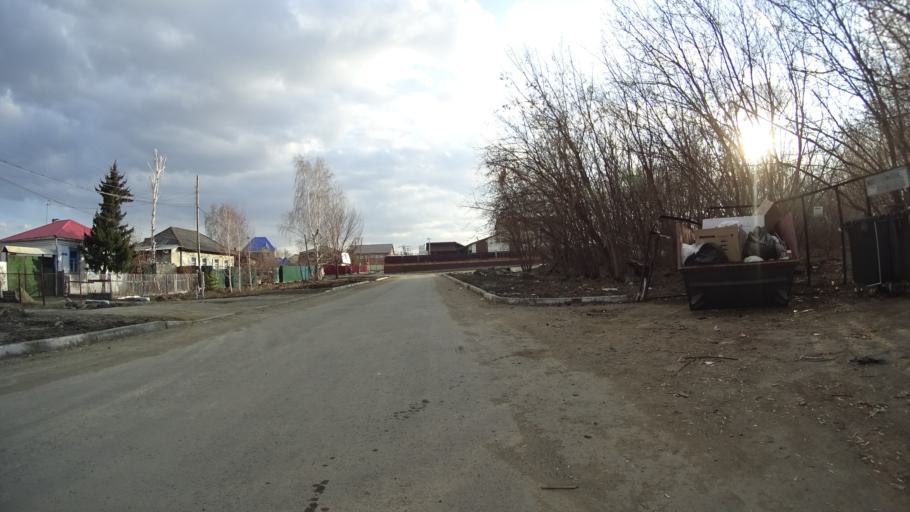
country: RU
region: Chelyabinsk
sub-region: Gorod Chelyabinsk
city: Chelyabinsk
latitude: 55.1335
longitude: 61.3881
